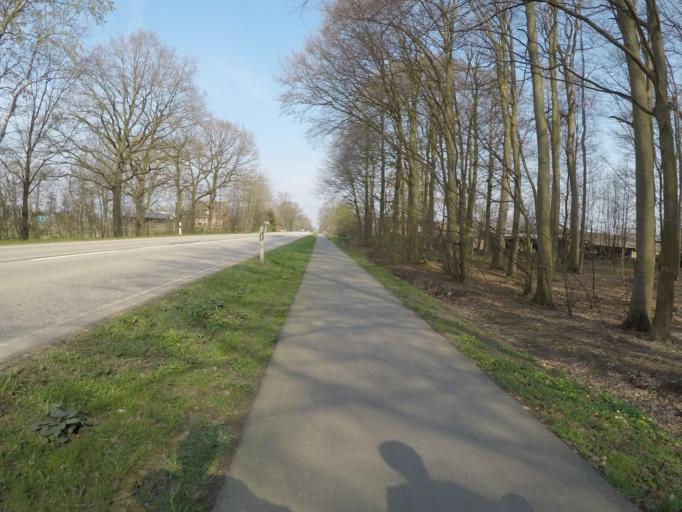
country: DE
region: Schleswig-Holstein
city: Seth
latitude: 53.8317
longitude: 10.2109
